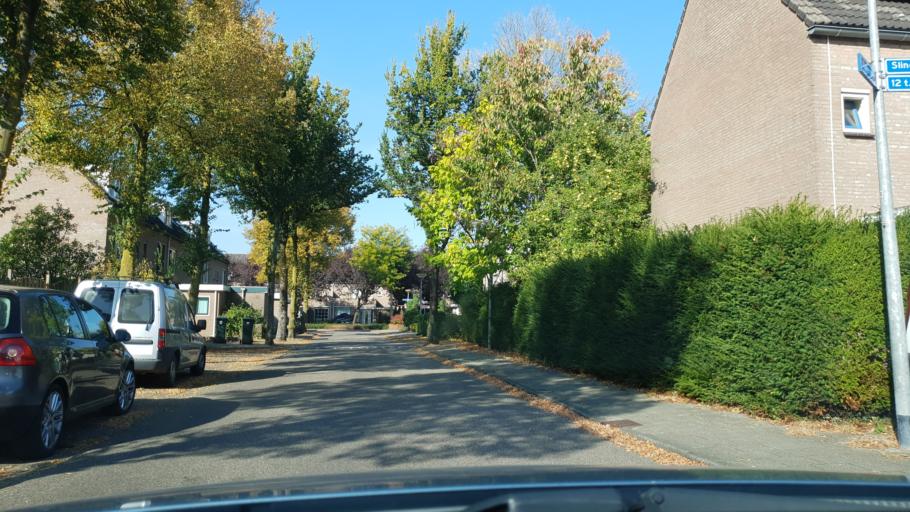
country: NL
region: Gelderland
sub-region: Gemeente Beuningen
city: Beuningen
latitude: 51.8625
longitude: 5.7679
